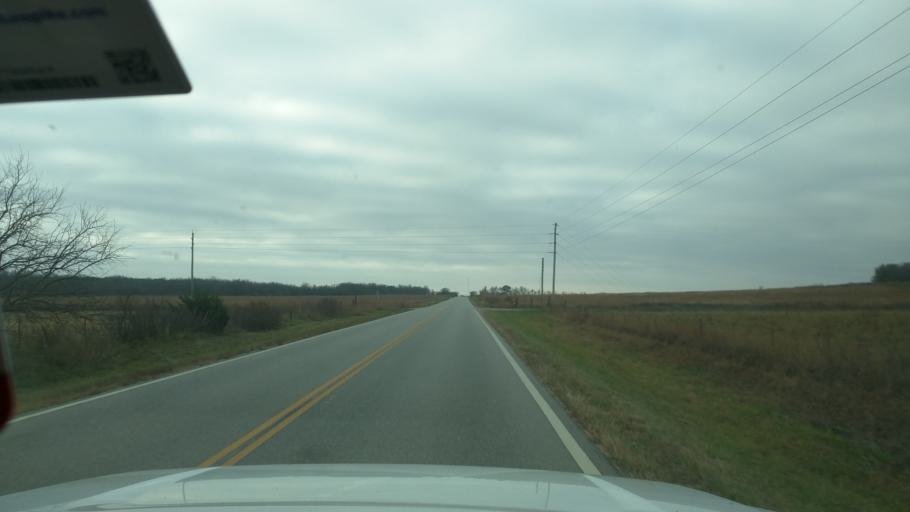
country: US
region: Kansas
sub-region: Greenwood County
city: Eureka
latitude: 37.6653
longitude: -96.2345
